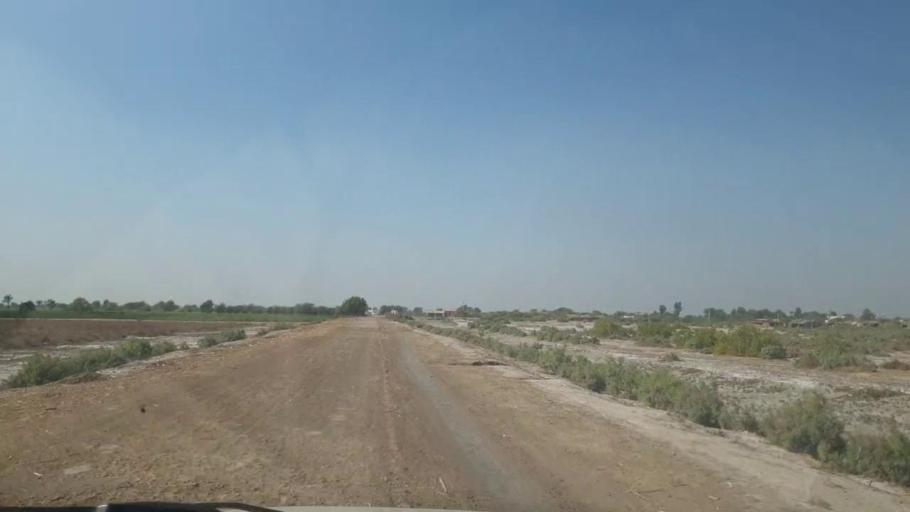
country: PK
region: Sindh
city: Mirpur Khas
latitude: 25.4763
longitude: 69.1204
